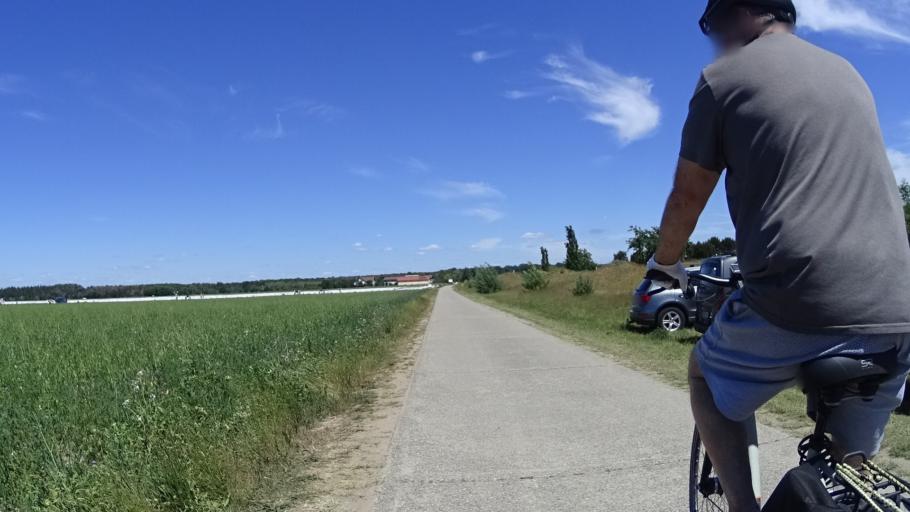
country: DE
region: Hesse
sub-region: Regierungsbezirk Darmstadt
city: Buttelborn
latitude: 49.9368
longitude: 8.5500
